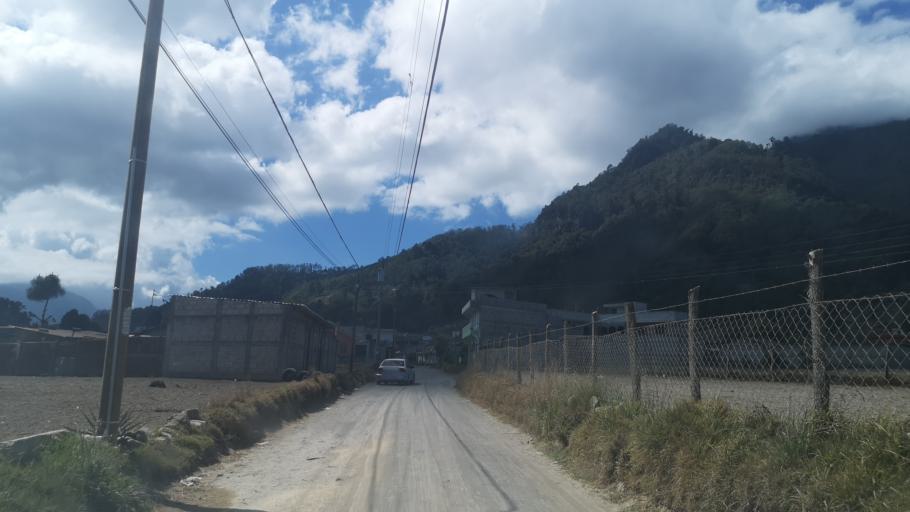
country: GT
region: Quetzaltenango
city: Almolonga
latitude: 14.7871
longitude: -91.5387
